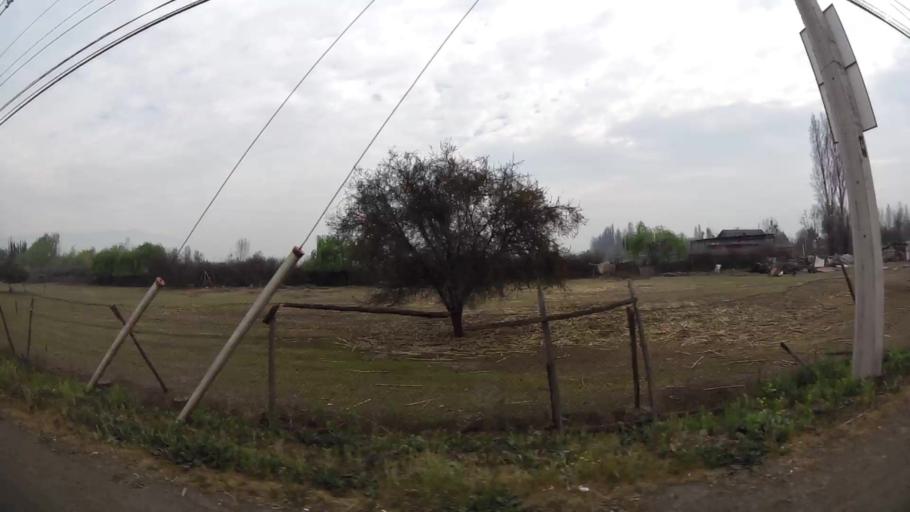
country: CL
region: Santiago Metropolitan
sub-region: Provincia de Chacabuco
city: Lampa
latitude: -33.2262
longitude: -70.7767
